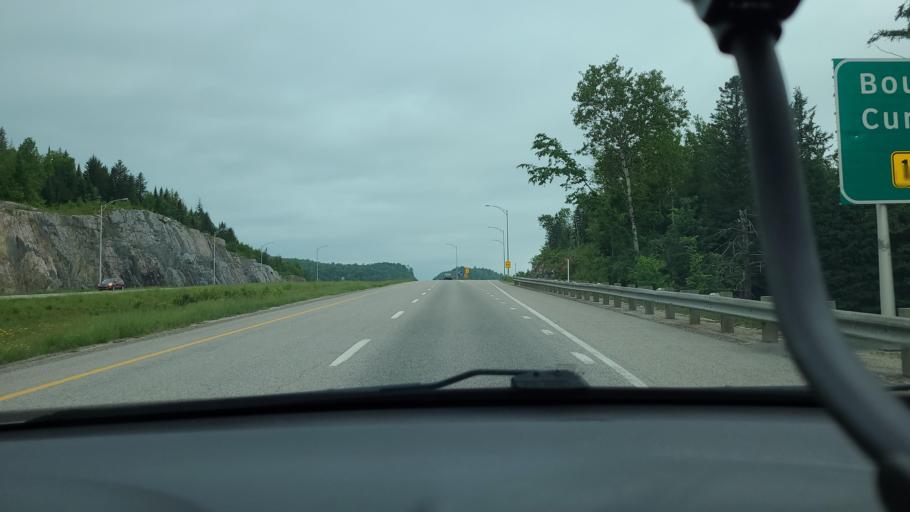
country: CA
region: Quebec
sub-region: Laurentides
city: Labelle
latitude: 46.2522
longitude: -74.7203
